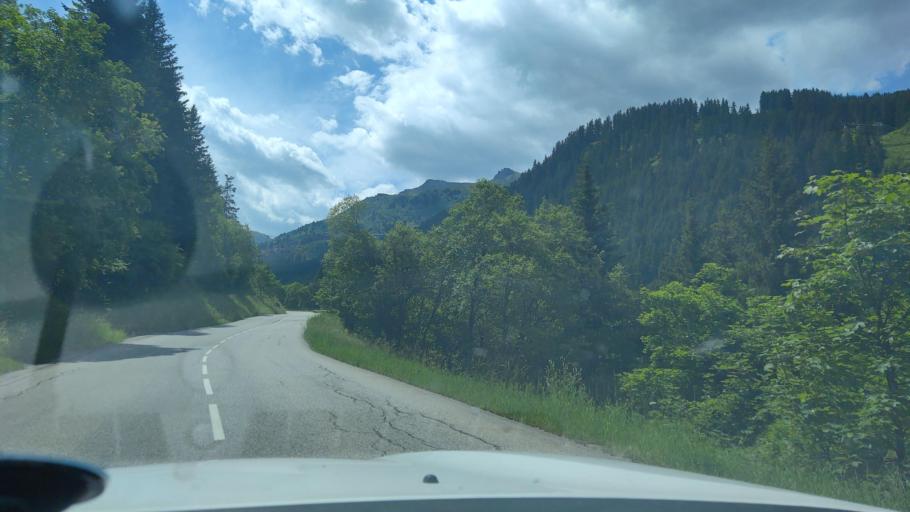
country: FR
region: Rhone-Alpes
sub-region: Departement de la Savoie
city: Meribel
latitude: 45.3888
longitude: 6.5701
